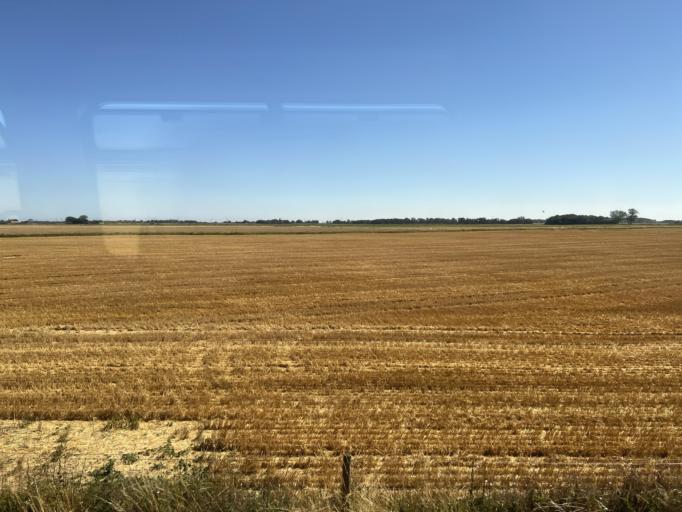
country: GB
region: England
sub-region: Lincolnshire
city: Spilsby
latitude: 53.1190
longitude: 0.1347
